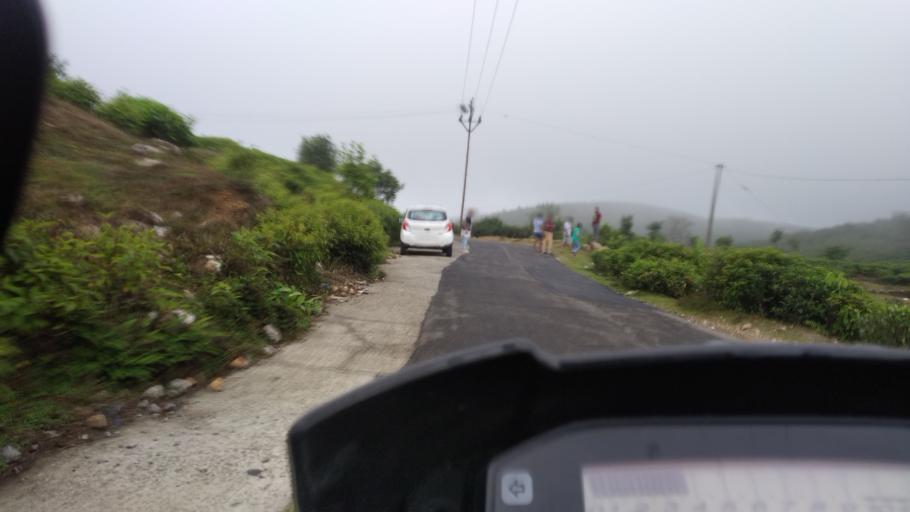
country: IN
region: Kerala
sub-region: Kottayam
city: Erattupetta
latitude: 9.6311
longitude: 76.9392
